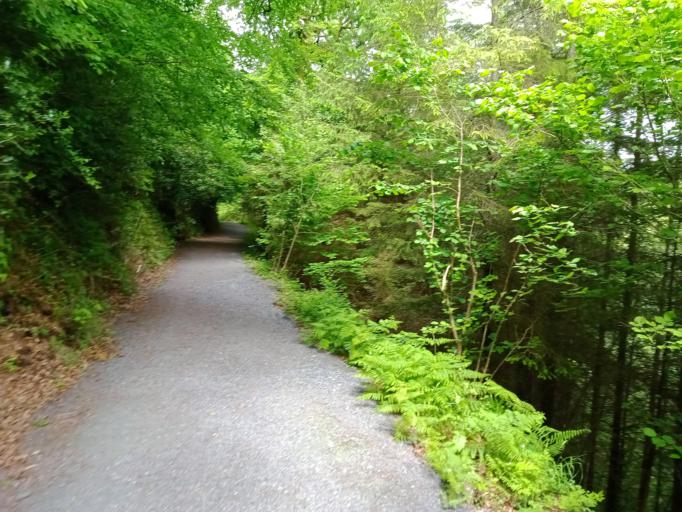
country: IE
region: Leinster
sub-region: Kilkenny
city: Thomastown
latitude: 52.4747
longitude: -7.0464
